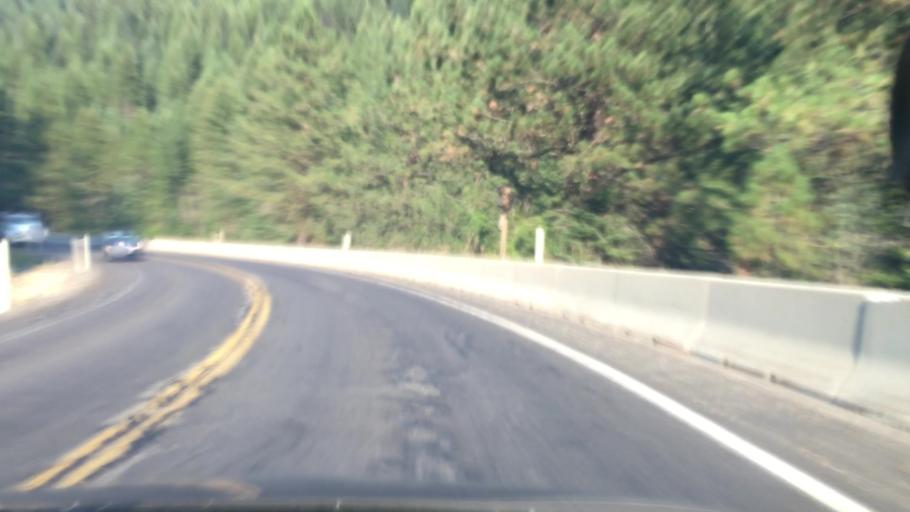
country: US
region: Idaho
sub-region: Valley County
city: Cascade
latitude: 44.2612
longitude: -116.0698
